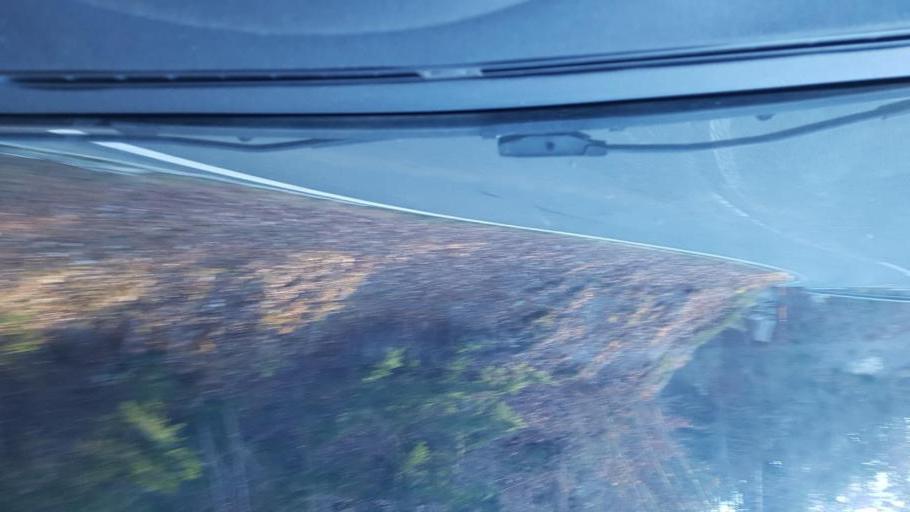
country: AT
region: Carinthia
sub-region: Politischer Bezirk Klagenfurt Land
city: Ferlach
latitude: 46.4905
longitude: 14.2778
